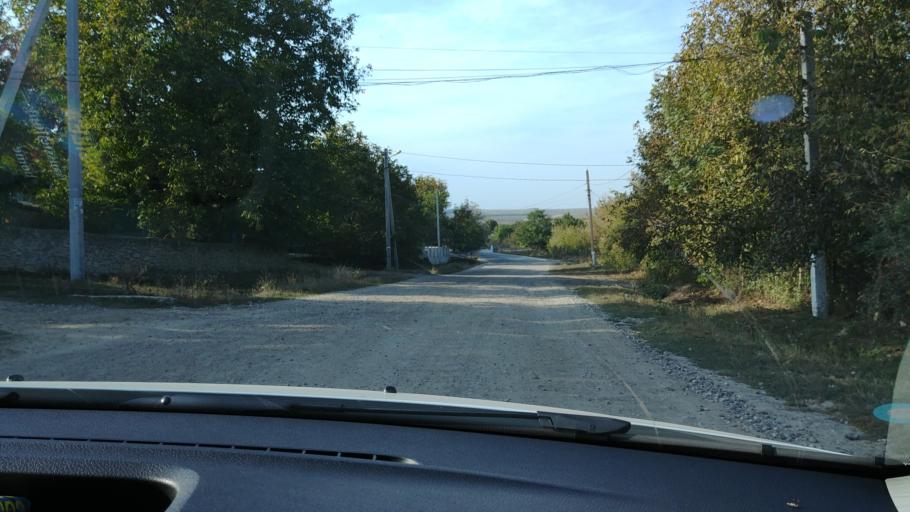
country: MD
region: Rezina
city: Rezina
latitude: 47.7478
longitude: 28.8849
